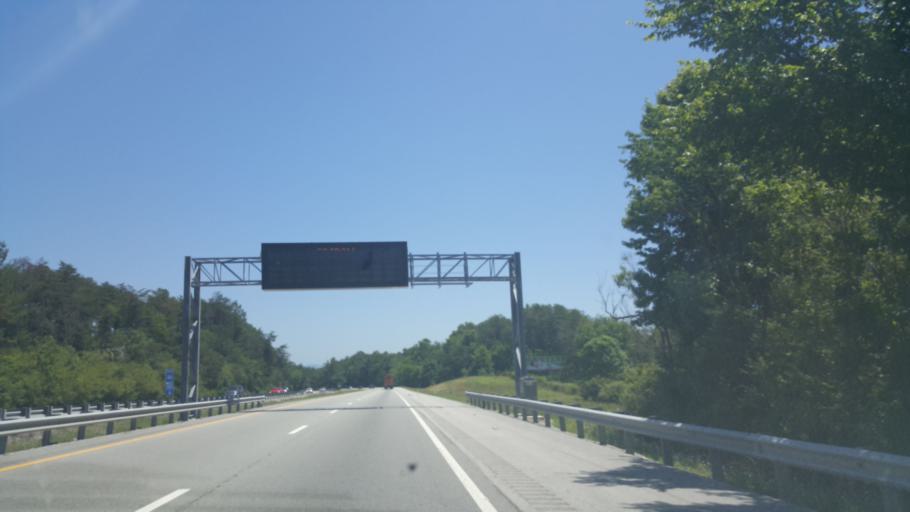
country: US
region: Tennessee
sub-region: Roane County
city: Rockwood
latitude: 35.8848
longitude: -84.8099
